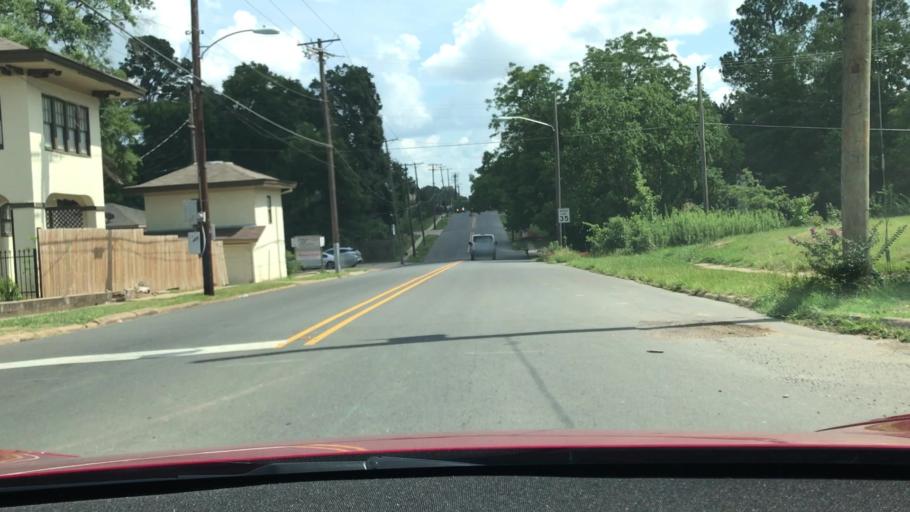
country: US
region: Louisiana
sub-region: Bossier Parish
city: Bossier City
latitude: 32.4963
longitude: -93.7333
